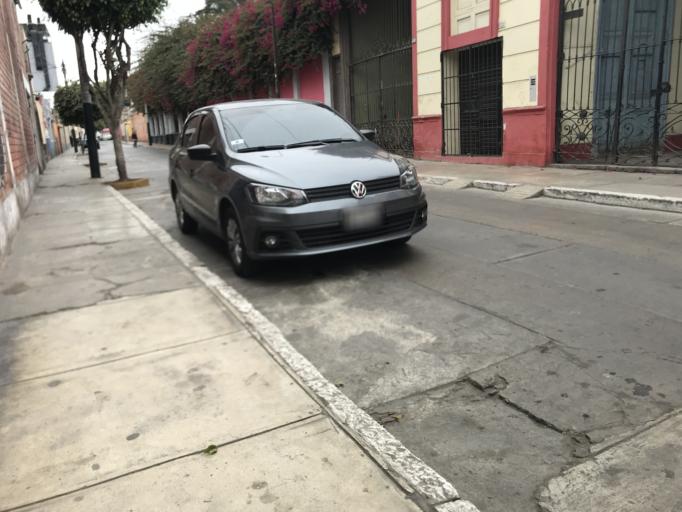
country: PE
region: Lima
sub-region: Lima
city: Surco
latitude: -12.1448
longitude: -77.0184
